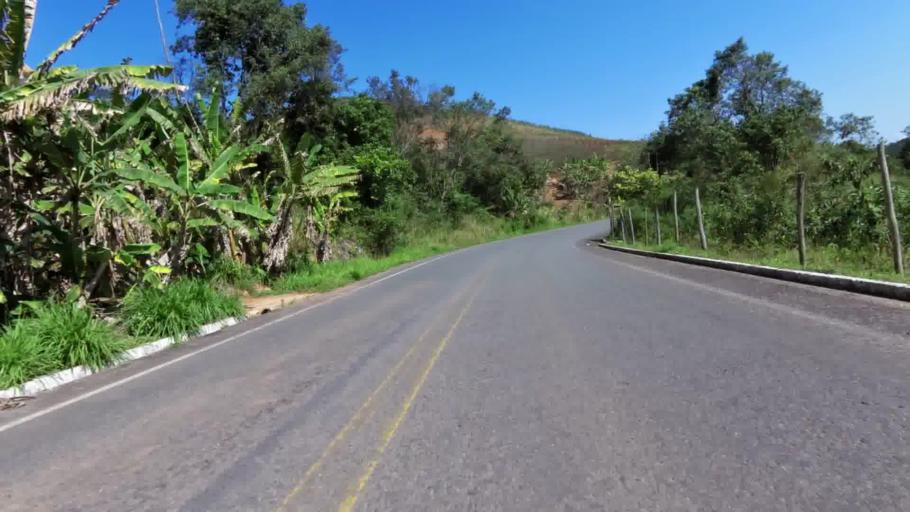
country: BR
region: Espirito Santo
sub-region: Alfredo Chaves
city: Alfredo Chaves
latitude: -20.5471
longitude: -40.7885
